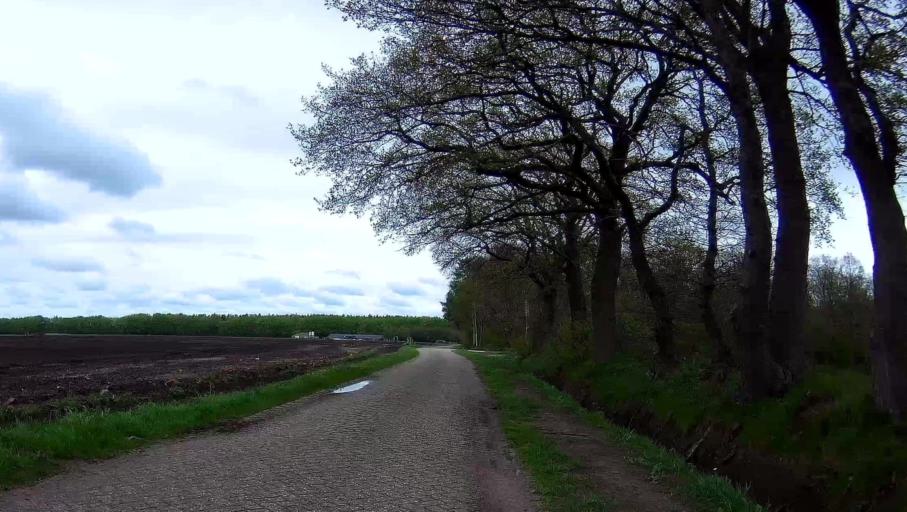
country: NL
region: Drenthe
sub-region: Gemeente Borger-Odoorn
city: Borger
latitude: 52.9448
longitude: 6.7787
